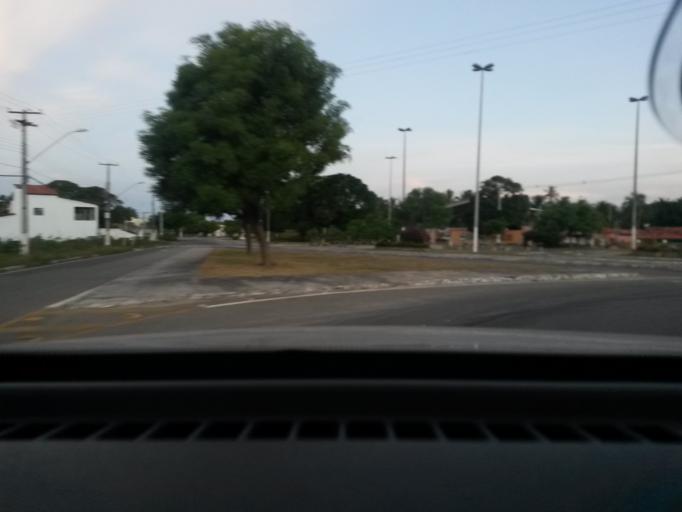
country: BR
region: Sergipe
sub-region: Sao Cristovao
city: Sao Cristovao
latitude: -11.0981
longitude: -37.1432
